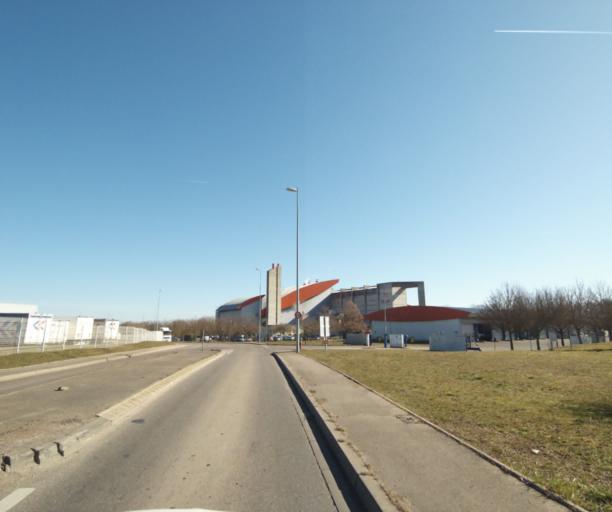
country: FR
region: Lorraine
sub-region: Departement de Meurthe-et-Moselle
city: Fleville-devant-Nancy
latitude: 48.6158
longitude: 6.1952
